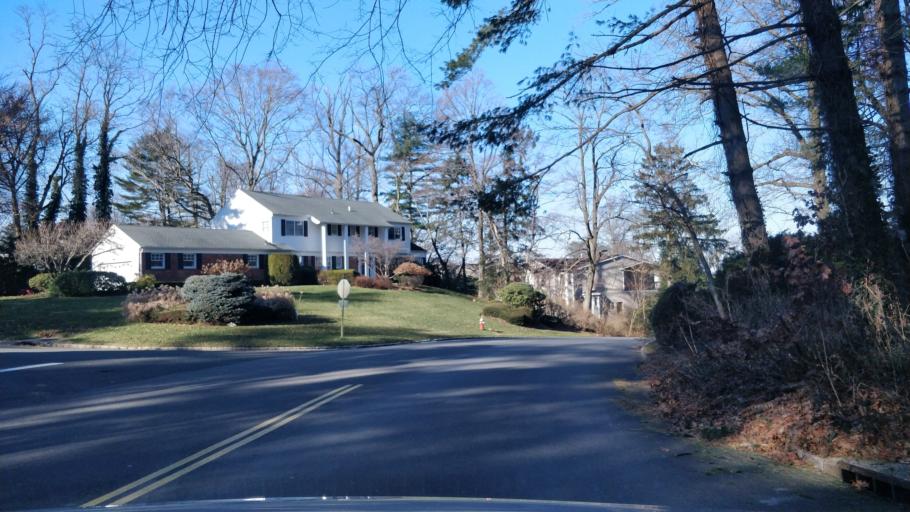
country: US
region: New York
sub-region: Nassau County
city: East Hills
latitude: 40.8000
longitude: -73.6366
